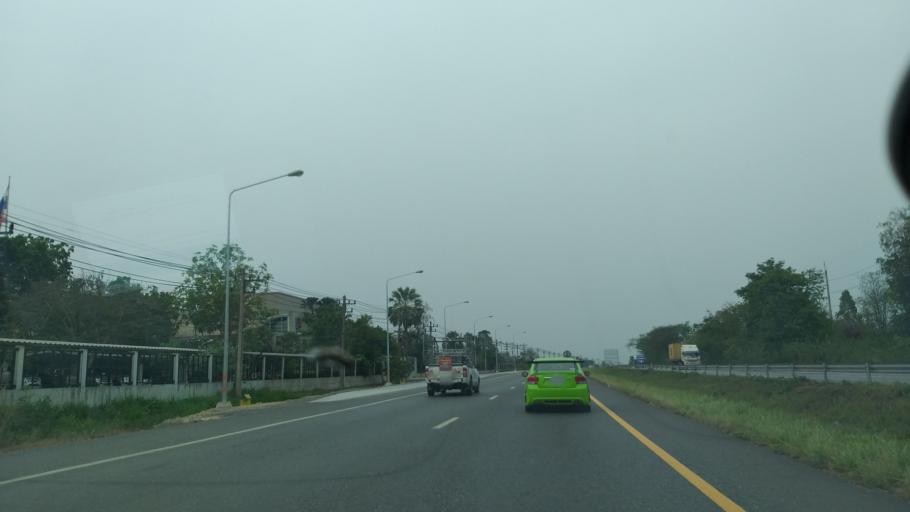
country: TH
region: Chon Buri
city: Ko Chan
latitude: 13.3481
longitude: 101.2708
